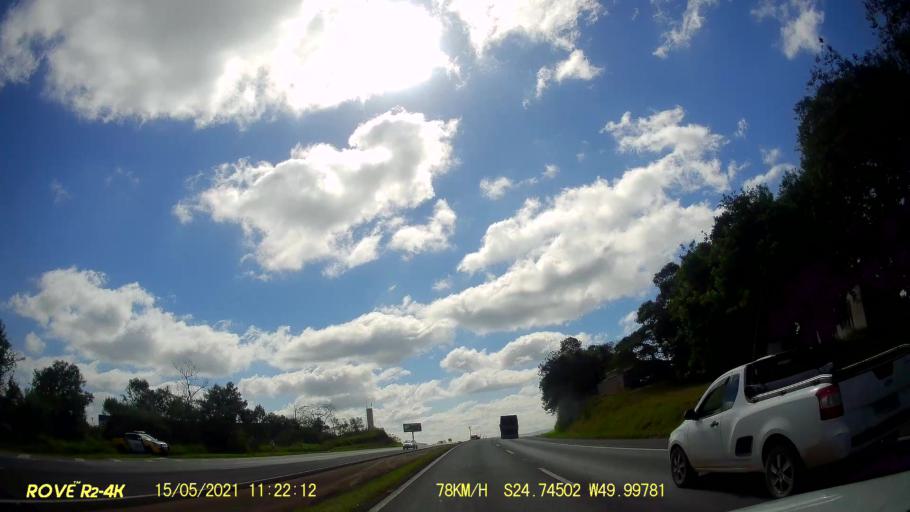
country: BR
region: Parana
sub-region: Castro
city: Castro
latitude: -24.7451
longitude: -49.9979
